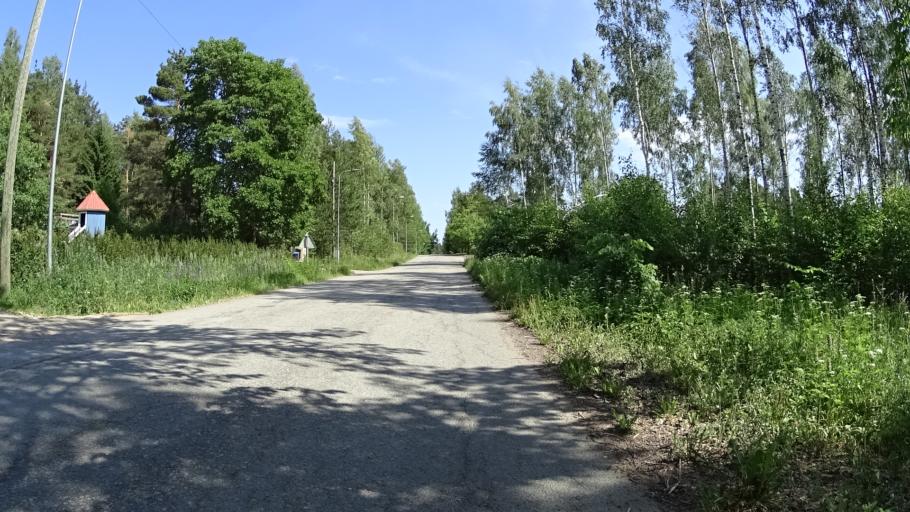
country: FI
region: Uusimaa
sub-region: Raaseporin
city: Karis
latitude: 60.0835
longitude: 23.6552
